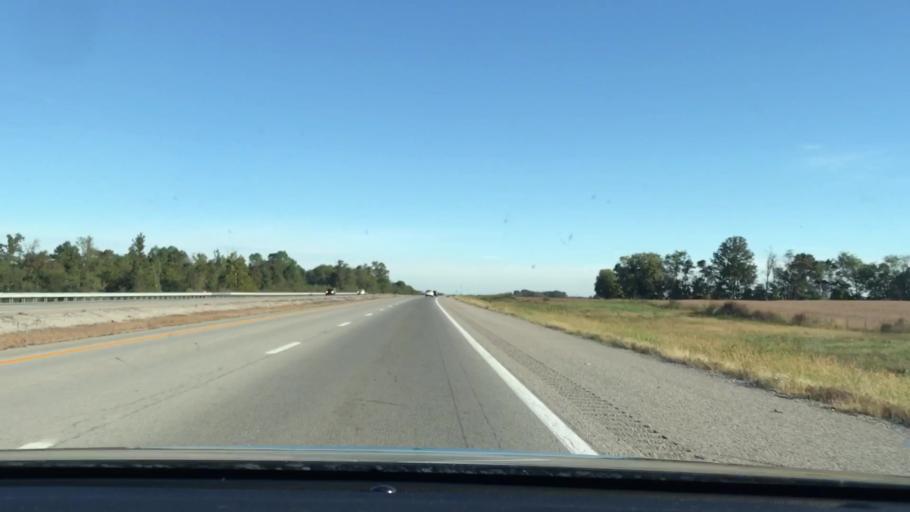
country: US
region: Kentucky
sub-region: Christian County
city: Hopkinsville
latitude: 36.7767
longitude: -87.4981
